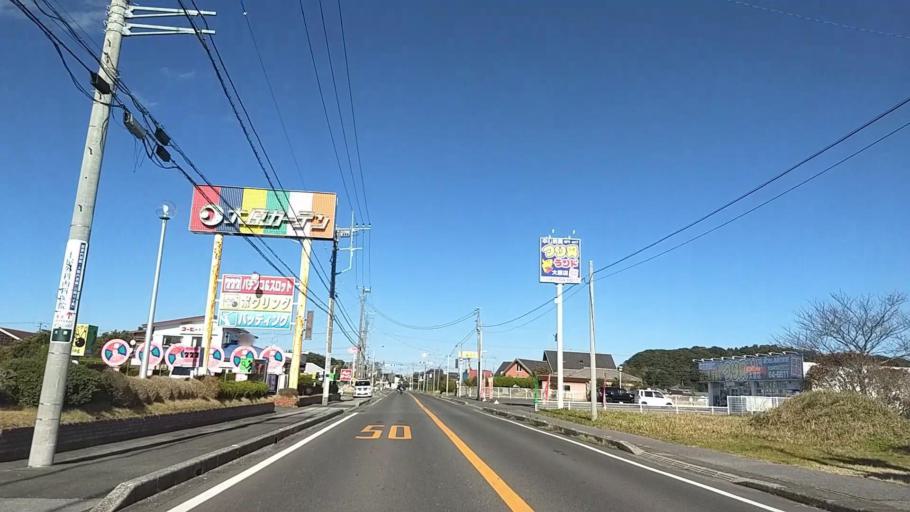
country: JP
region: Chiba
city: Ohara
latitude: 35.2414
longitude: 140.3922
